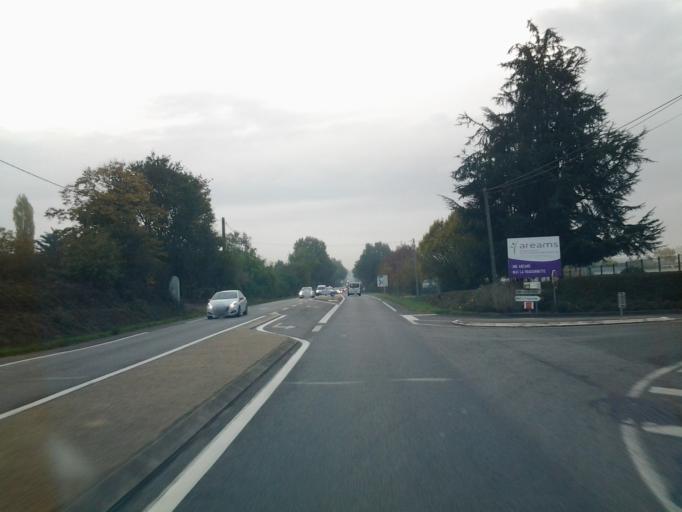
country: FR
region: Pays de la Loire
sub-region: Departement de la Vendee
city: Nesmy
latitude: 46.6245
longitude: -1.3724
